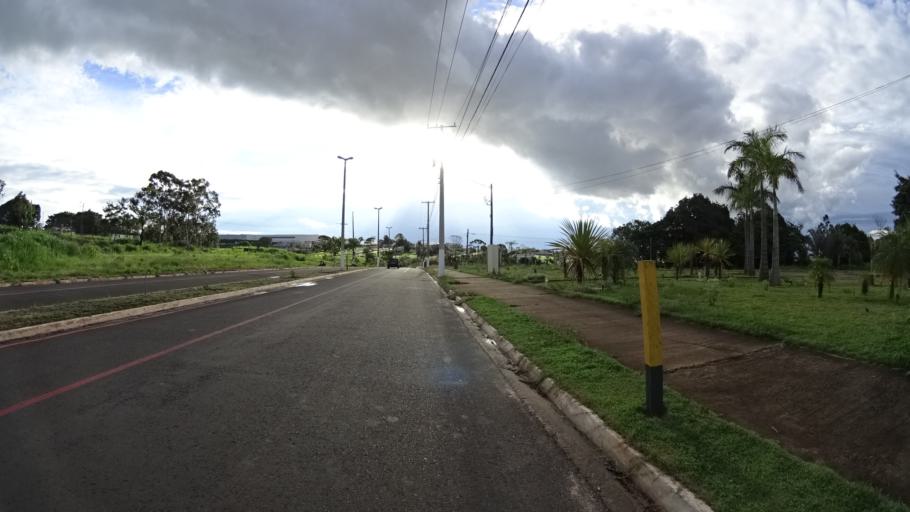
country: BR
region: Sao Paulo
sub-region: Marilia
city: Marilia
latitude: -22.2268
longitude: -49.9045
